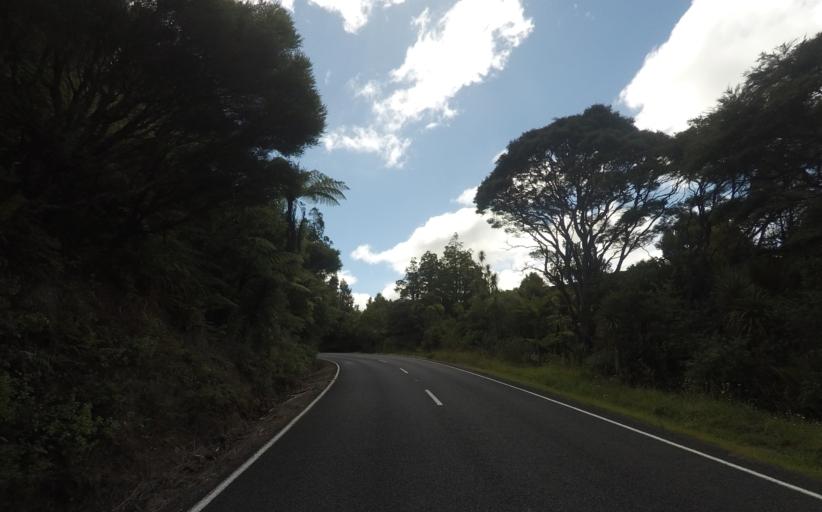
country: NZ
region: Auckland
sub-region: Auckland
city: Muriwai Beach
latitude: -36.8618
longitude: 174.5177
